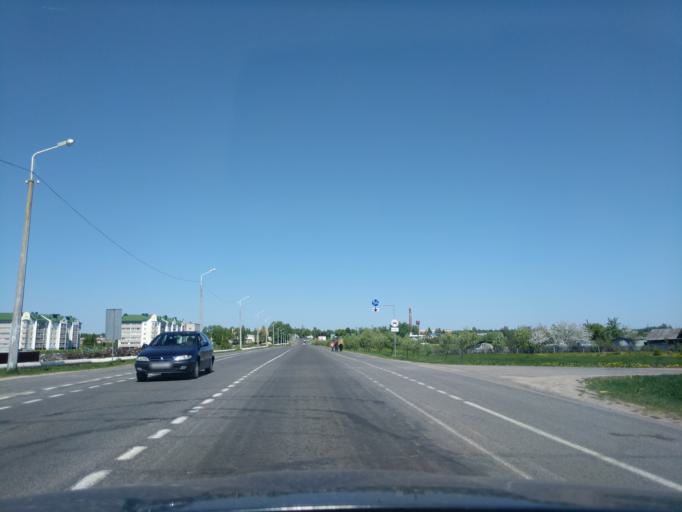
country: BY
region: Minsk
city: Myadzyel
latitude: 54.8775
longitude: 26.9408
